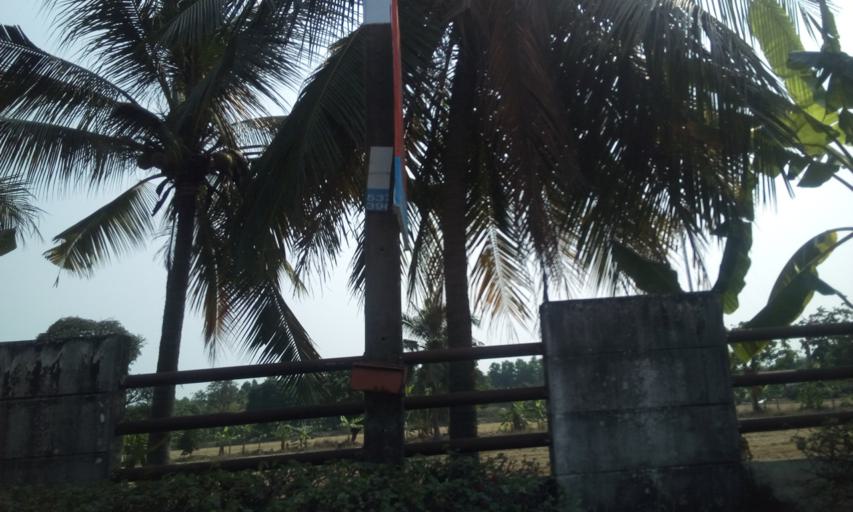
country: TH
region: Pathum Thani
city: Ban Lam Luk Ka
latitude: 13.9716
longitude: 100.7475
